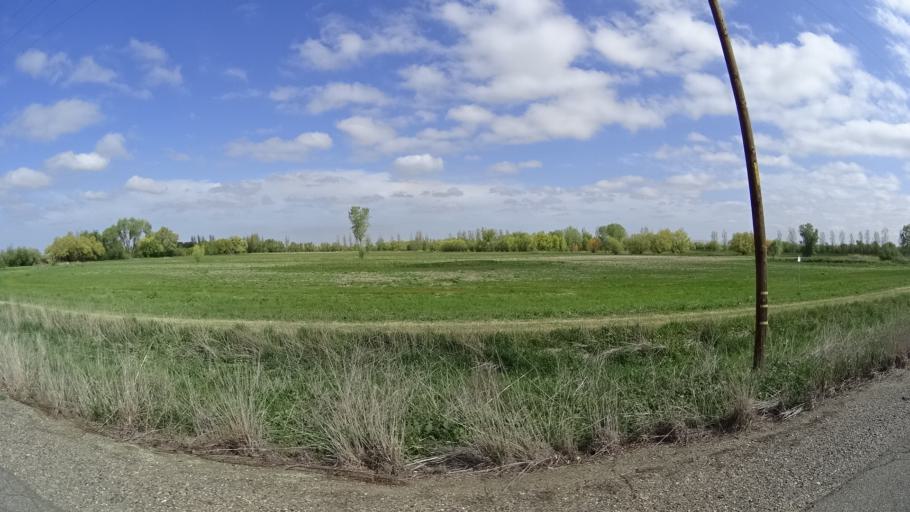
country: US
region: California
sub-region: Butte County
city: Biggs
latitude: 39.4203
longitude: -121.9202
